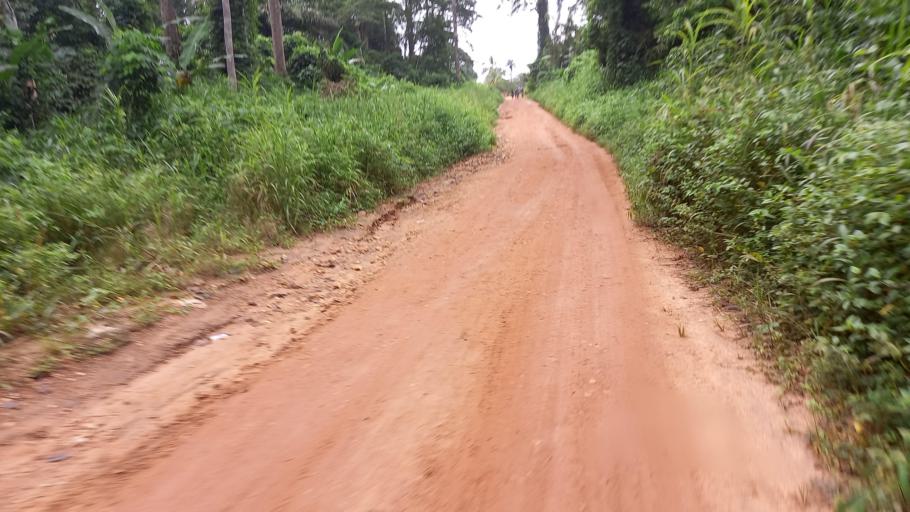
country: SL
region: Eastern Province
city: Kailahun
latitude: 8.2494
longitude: -10.5205
